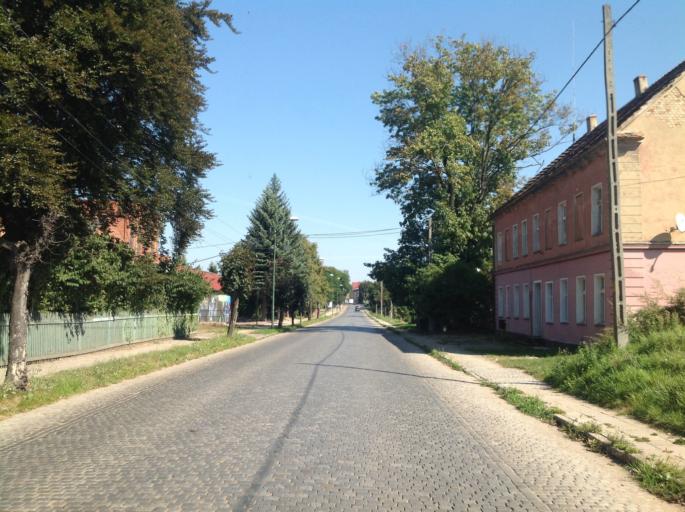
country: PL
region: Lower Silesian Voivodeship
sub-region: Powiat zabkowicki
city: Ziebice
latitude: 50.5925
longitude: 17.0326
